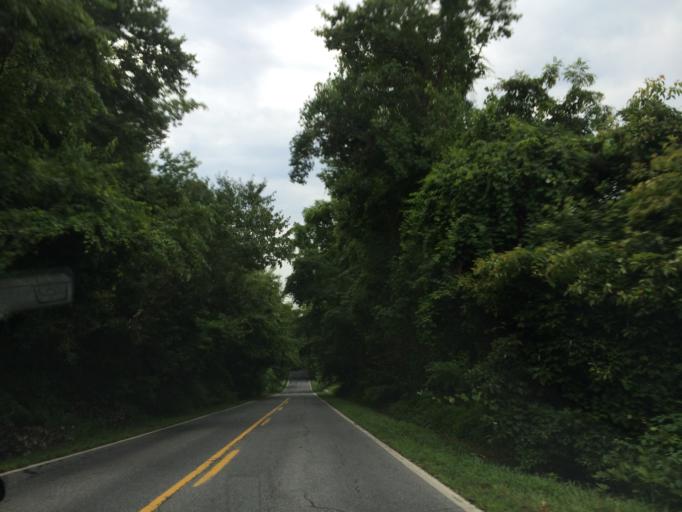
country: US
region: Maryland
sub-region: Montgomery County
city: Ashton-Sandy Spring
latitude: 39.1925
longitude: -77.0243
